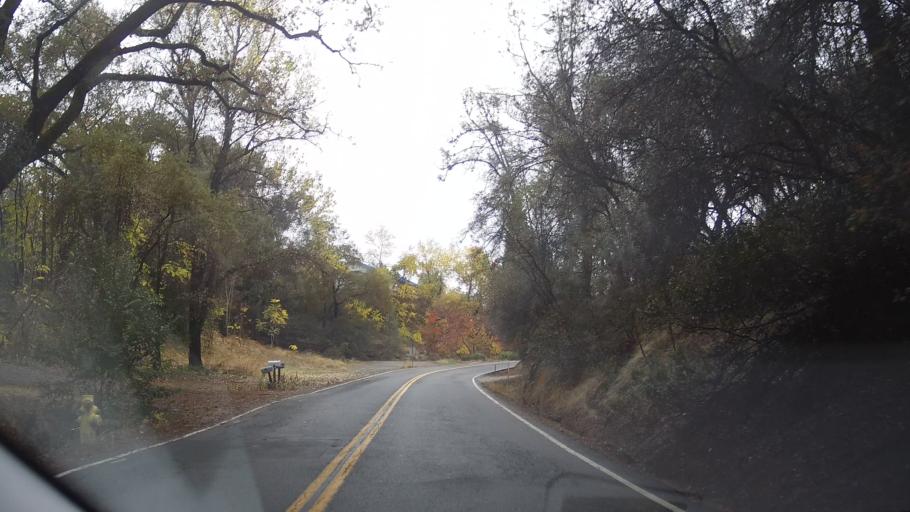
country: US
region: California
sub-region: Placer County
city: North Auburn
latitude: 38.9155
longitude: -121.0778
